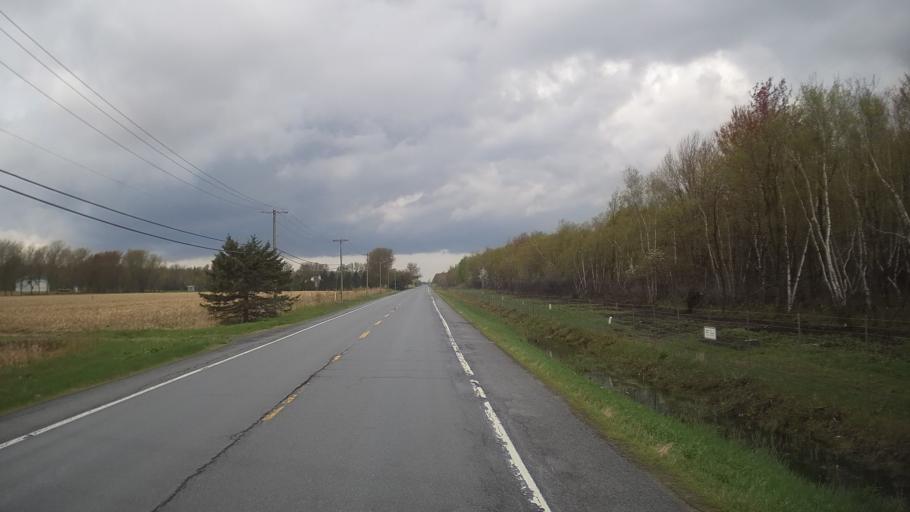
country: CA
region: Quebec
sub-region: Monteregie
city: Farnham
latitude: 45.2974
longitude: -73.0278
